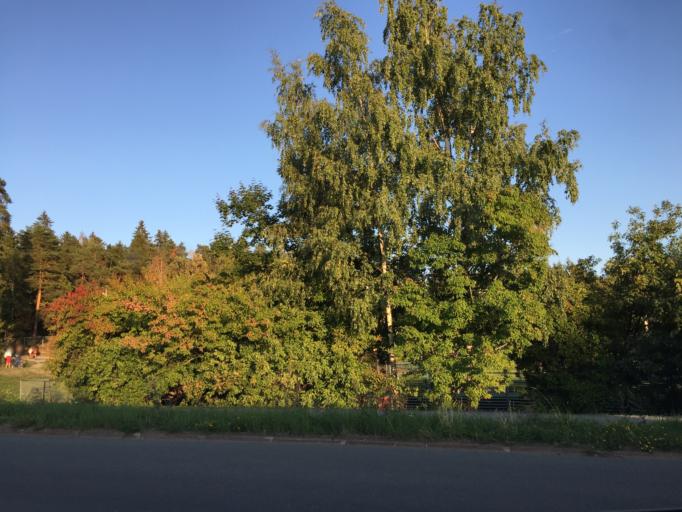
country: NO
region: Akershus
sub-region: Baerum
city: Lysaker
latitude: 59.8879
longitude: 10.6200
